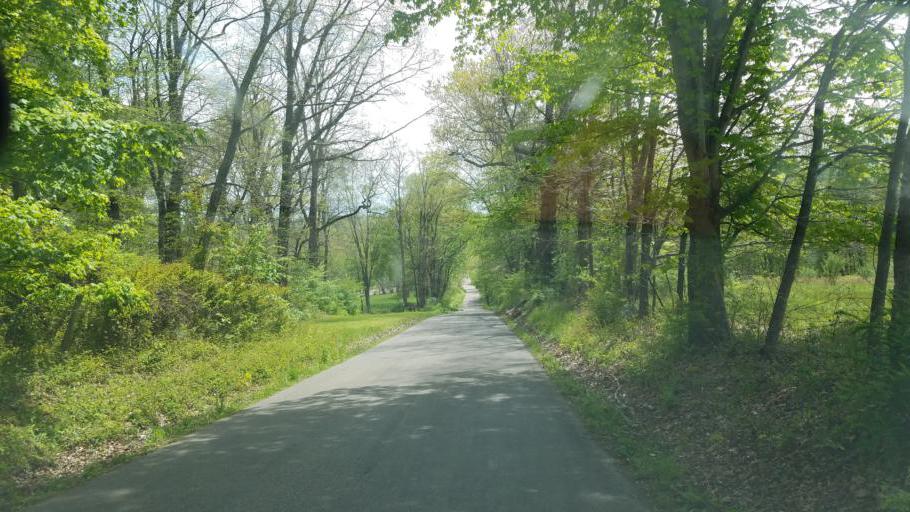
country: US
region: Ohio
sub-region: Knox County
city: Gambier
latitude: 40.3817
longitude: -82.3708
